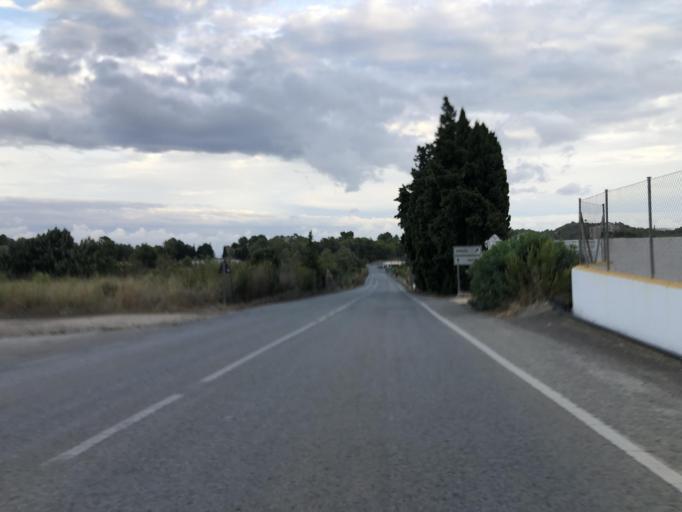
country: ES
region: Valencia
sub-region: Provincia de Alicante
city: Polop
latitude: 38.6272
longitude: -0.1395
